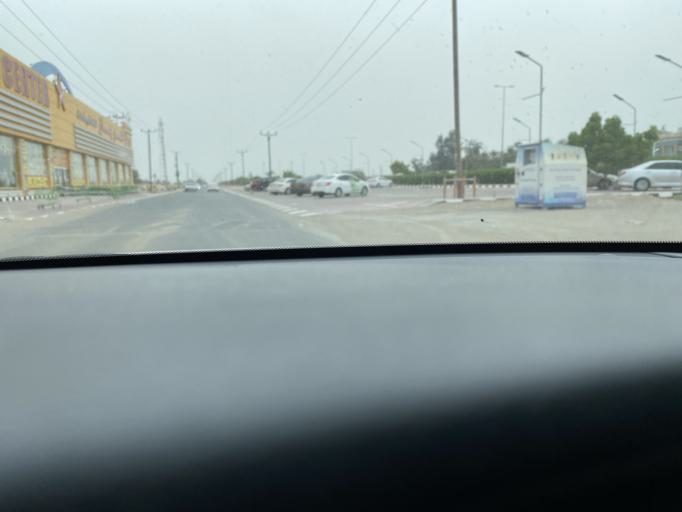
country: OM
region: Al Batinah
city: Barka'
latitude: 23.6962
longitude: 57.7844
